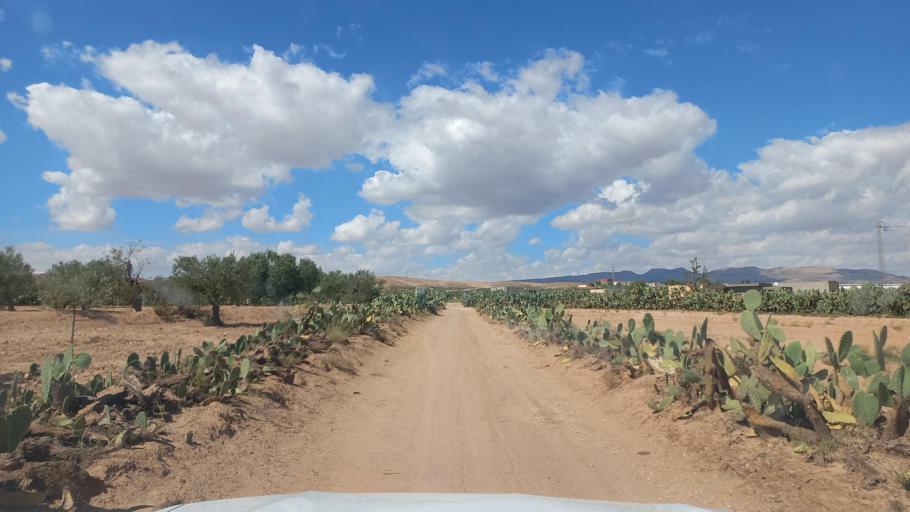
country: TN
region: Al Qasrayn
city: Sbiba
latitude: 35.3552
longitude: 9.0185
